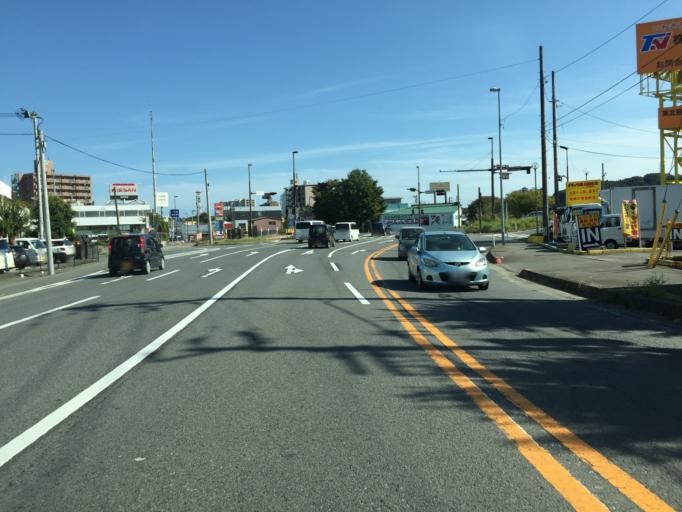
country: JP
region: Fukushima
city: Iwaki
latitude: 37.0536
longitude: 140.8789
